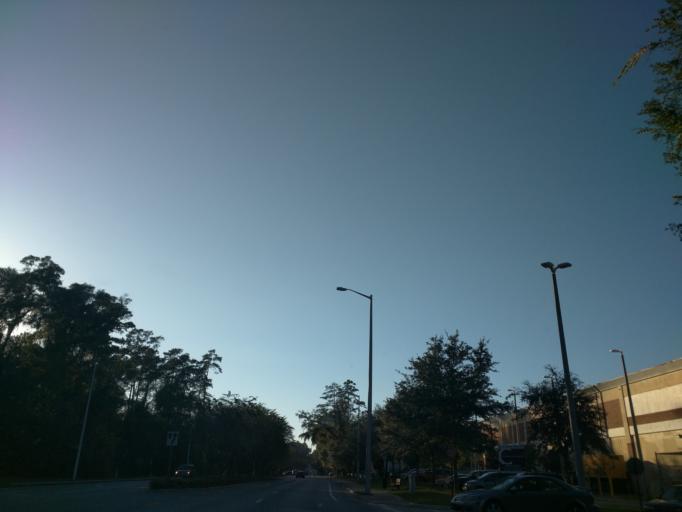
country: US
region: Florida
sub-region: Leon County
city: Tallahassee
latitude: 30.4419
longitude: -84.2471
